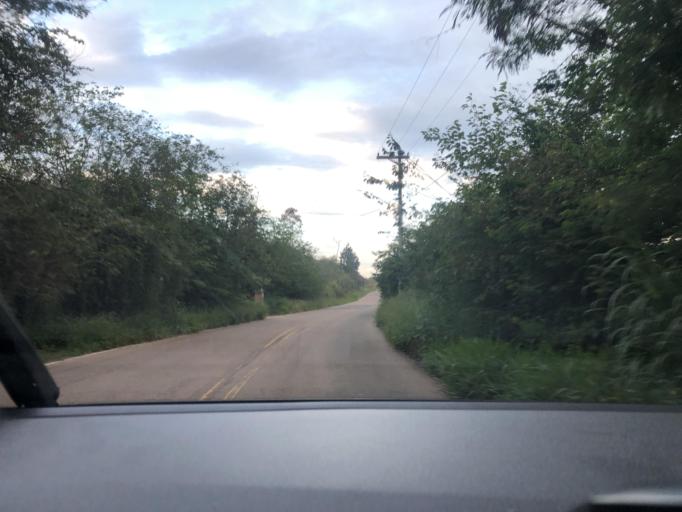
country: BR
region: Sao Paulo
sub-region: Louveira
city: Louveira
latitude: -23.1254
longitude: -46.9164
